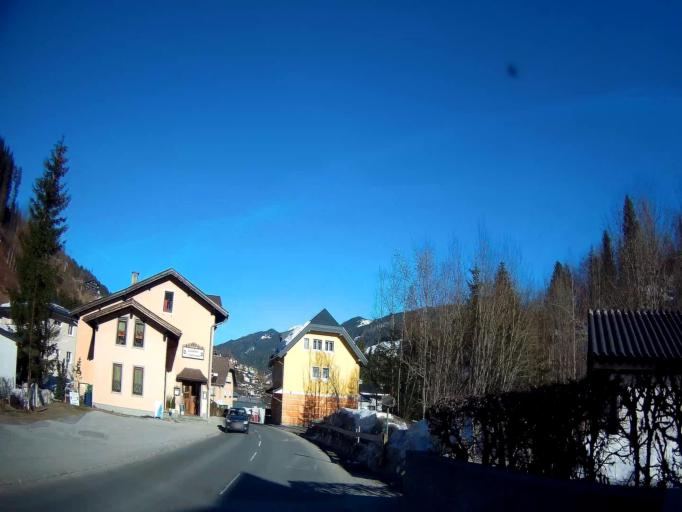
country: AT
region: Salzburg
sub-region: Politischer Bezirk Sankt Johann im Pongau
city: Muhlbach am Hochkonig
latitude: 47.3778
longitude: 13.1186
